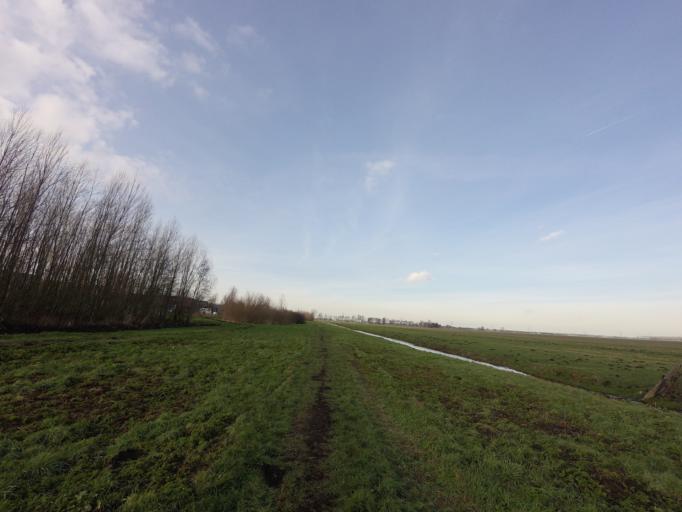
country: NL
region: Utrecht
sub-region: Gemeente Oudewater
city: Oudewater
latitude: 52.0355
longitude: 4.8710
